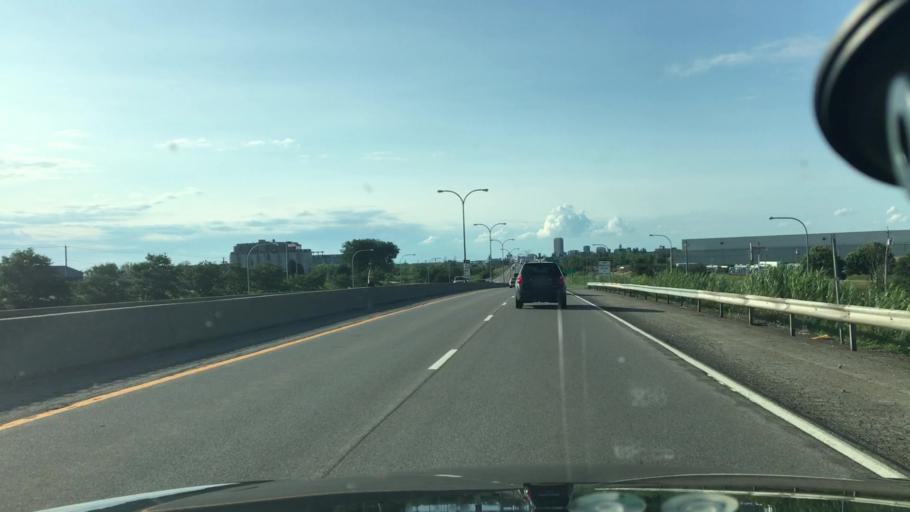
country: US
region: New York
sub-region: Erie County
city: Lackawanna
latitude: 42.8284
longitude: -78.8510
